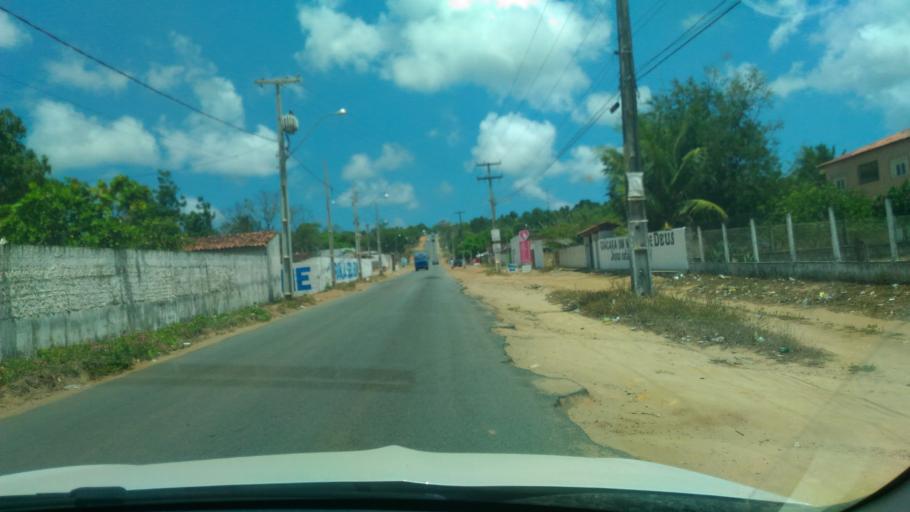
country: BR
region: Paraiba
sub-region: Conde
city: Conde
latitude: -7.2612
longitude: -34.9177
